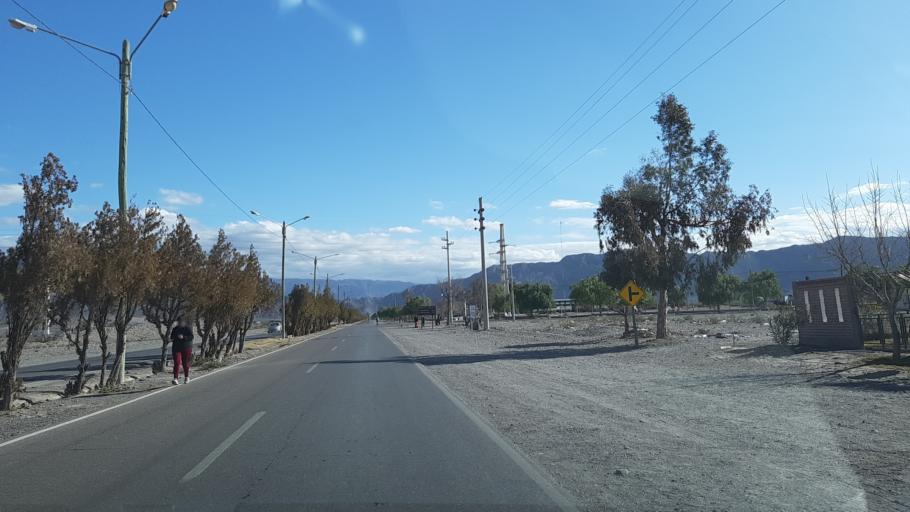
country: AR
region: San Juan
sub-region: Departamento de Rivadavia
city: Rivadavia
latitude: -31.5418
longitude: -68.6314
